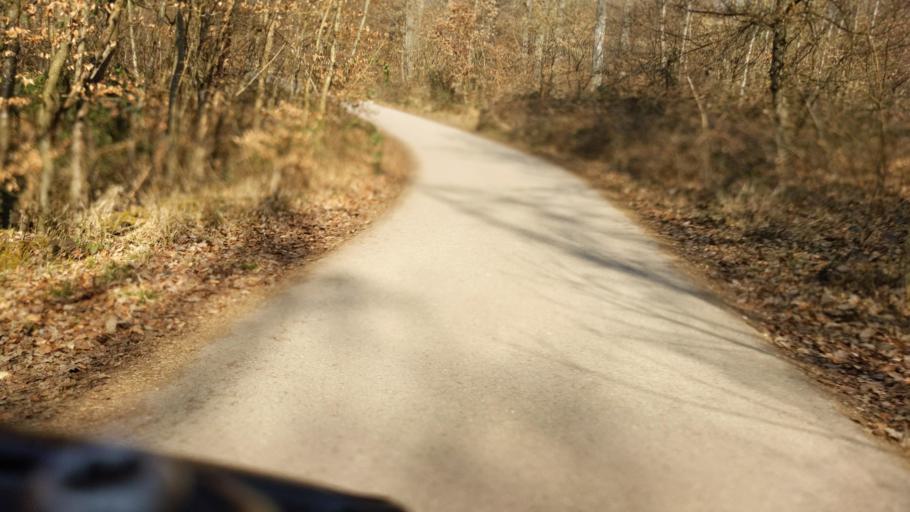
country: DE
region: Baden-Wuerttemberg
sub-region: Regierungsbezirk Stuttgart
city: Gerlingen
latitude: 48.7805
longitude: 9.0444
